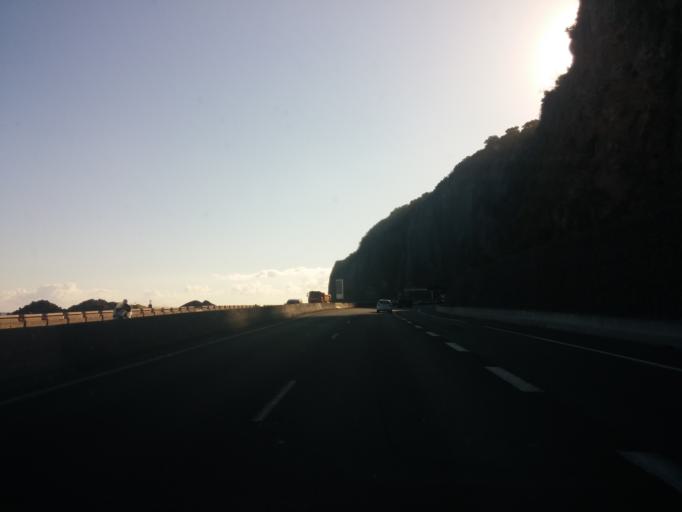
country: RE
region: Reunion
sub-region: Reunion
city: La Possession
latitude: -20.9211
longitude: 55.3461
